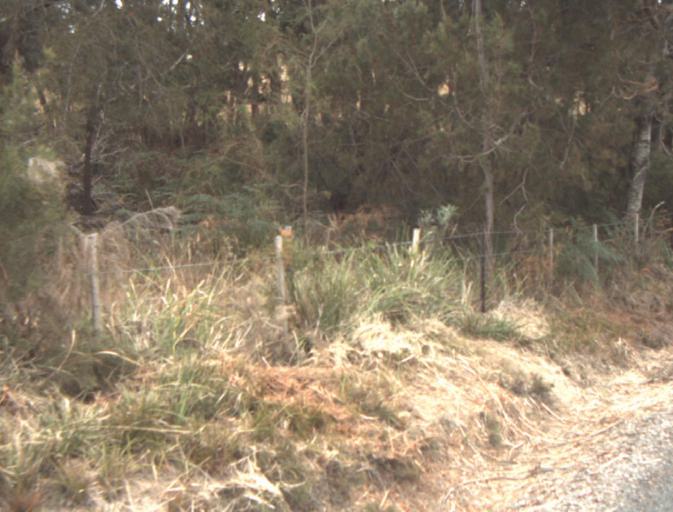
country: AU
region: Tasmania
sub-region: Launceston
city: Mayfield
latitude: -41.2832
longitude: 147.0159
